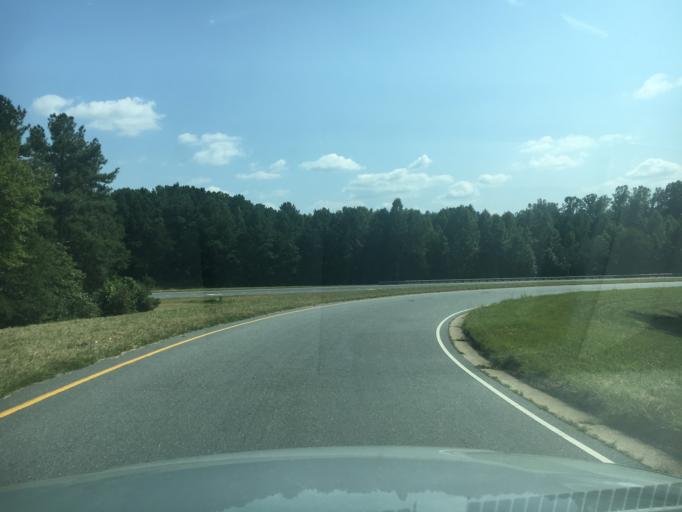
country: US
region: North Carolina
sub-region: Rutherford County
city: Forest City
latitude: 35.3124
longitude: -81.8709
